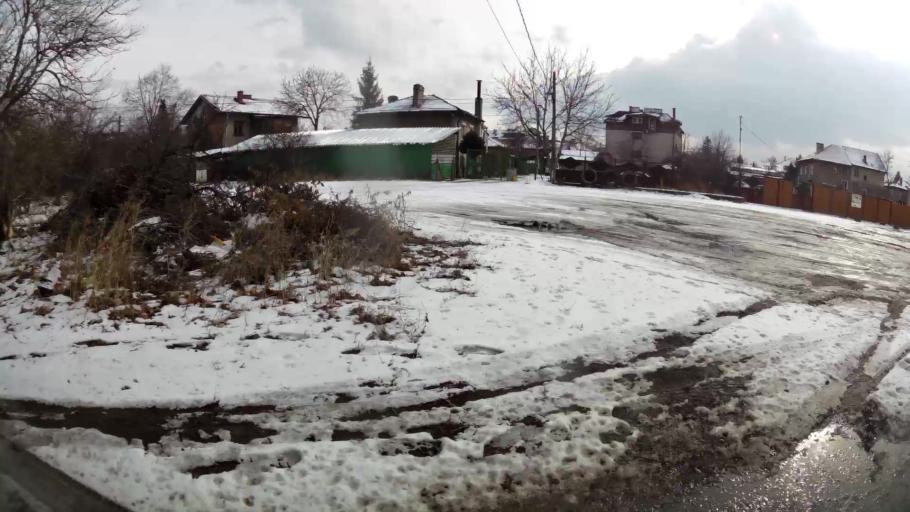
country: BG
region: Sofia-Capital
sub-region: Stolichna Obshtina
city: Sofia
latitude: 42.7077
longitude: 23.3811
